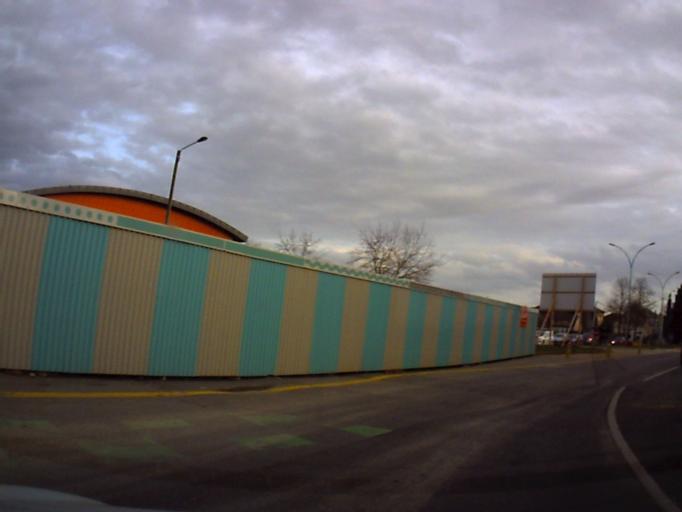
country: FR
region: Brittany
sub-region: Departement d'Ille-et-Vilaine
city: Rennes
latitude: 48.1235
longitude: -1.6515
